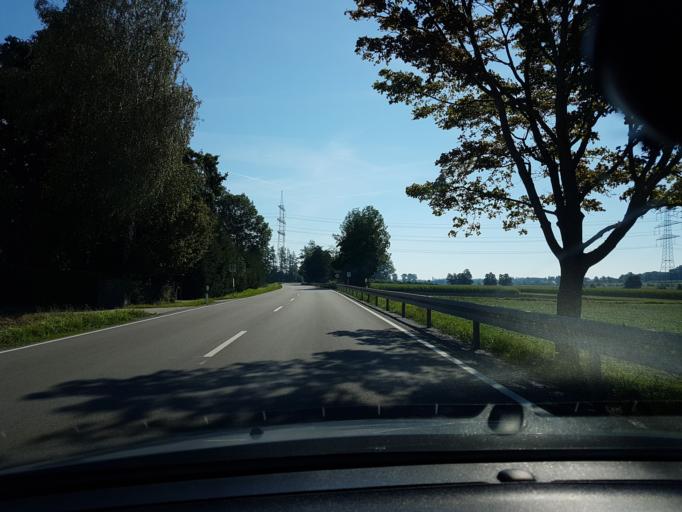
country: DE
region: Bavaria
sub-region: Upper Bavaria
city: Aham
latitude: 48.3469
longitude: 12.1497
